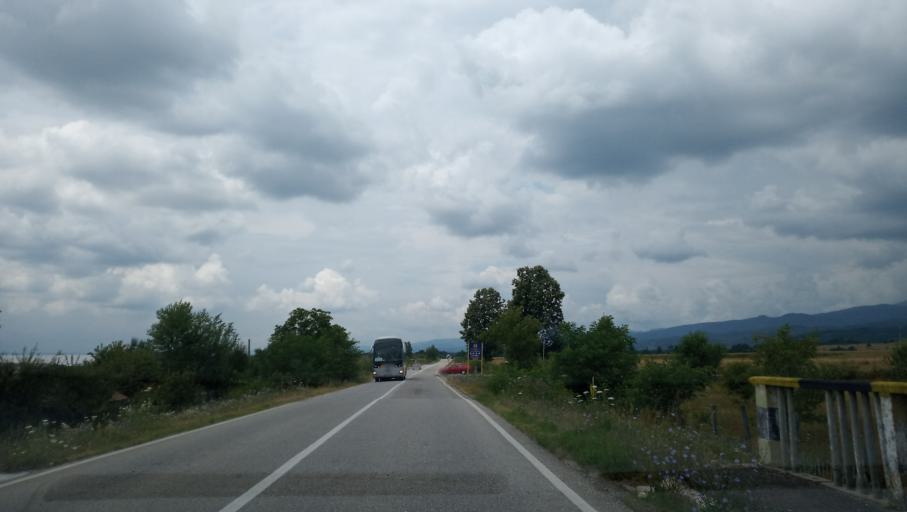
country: RO
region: Gorj
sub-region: Comuna Runcu
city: Valea Mare
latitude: 45.0869
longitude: 23.0926
